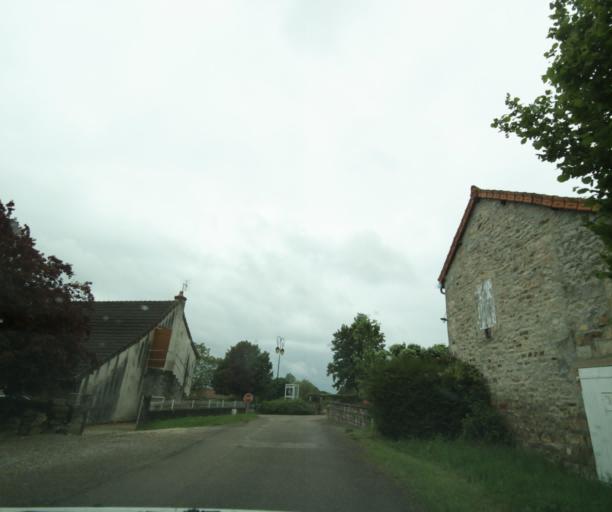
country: FR
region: Bourgogne
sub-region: Departement de Saone-et-Loire
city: Charolles
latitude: 46.4931
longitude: 4.2784
